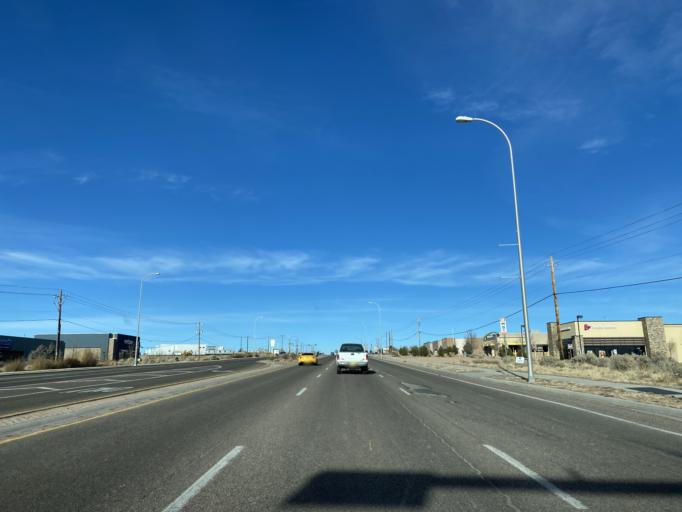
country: US
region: New Mexico
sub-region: Santa Fe County
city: Agua Fria
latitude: 35.6173
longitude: -106.0306
